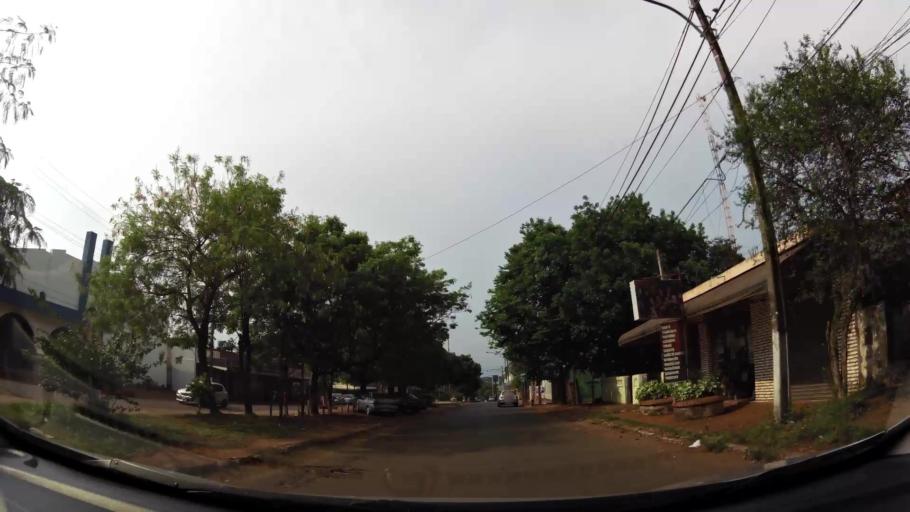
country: PY
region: Alto Parana
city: Ciudad del Este
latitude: -25.4987
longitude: -54.6512
